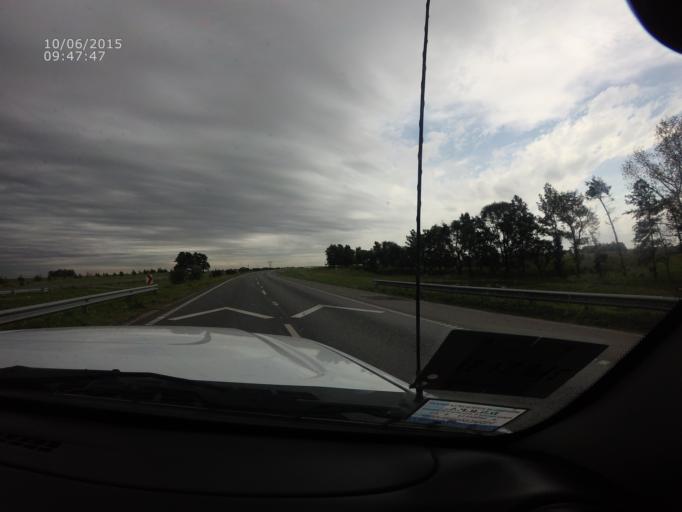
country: AR
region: Buenos Aires
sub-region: San Antonio de Areco
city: San Antonio de Areco
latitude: -34.0534
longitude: -59.3124
